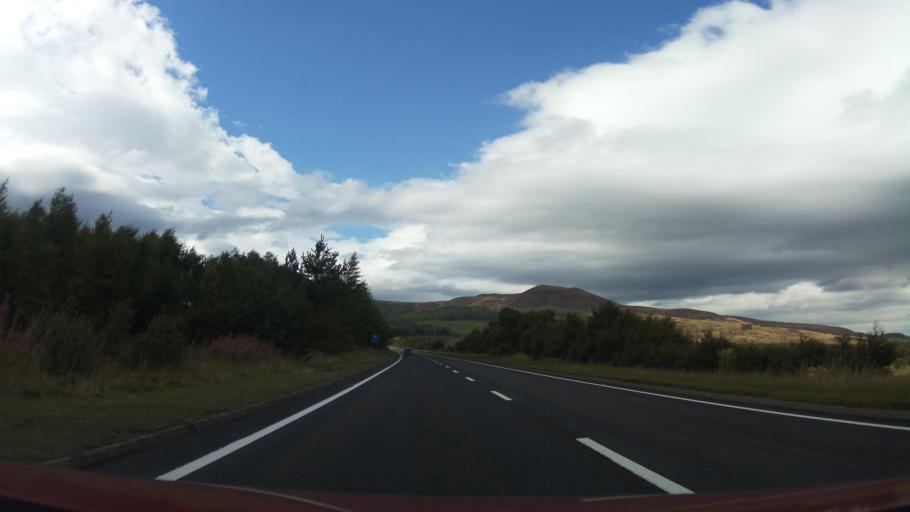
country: GB
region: Scotland
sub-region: Highland
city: Inverness
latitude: 57.3849
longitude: -4.0692
